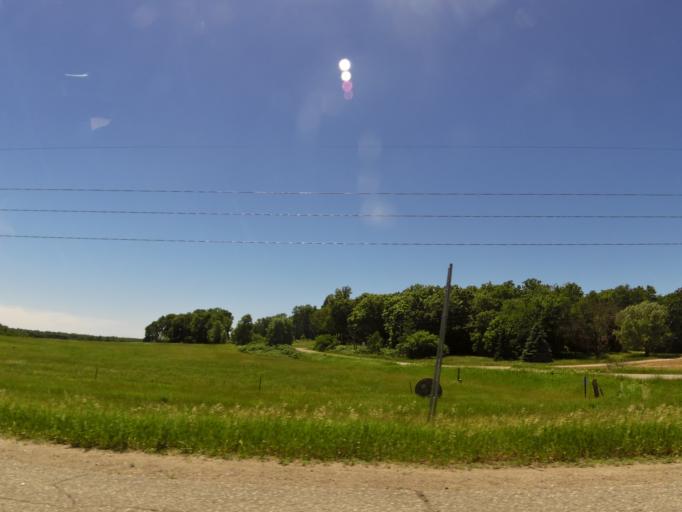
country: US
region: Minnesota
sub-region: Becker County
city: Frazee
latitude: 46.7389
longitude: -95.7526
